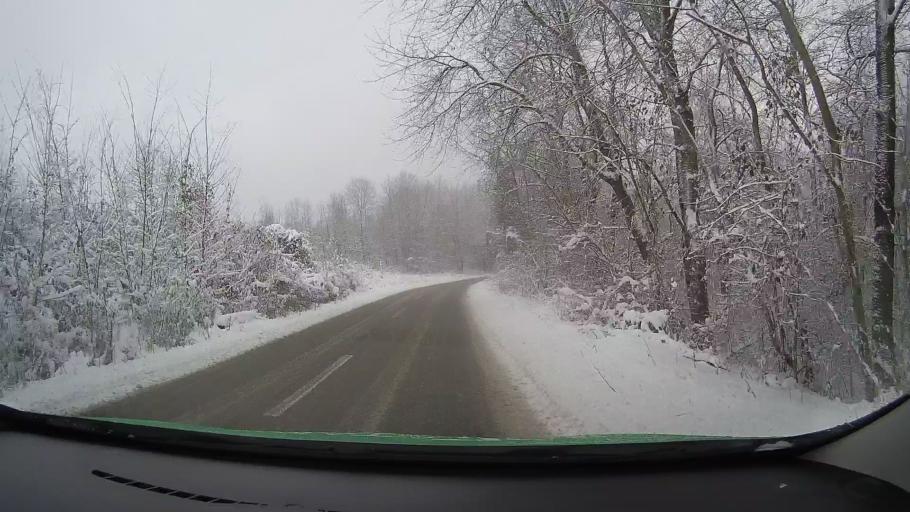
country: RO
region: Hunedoara
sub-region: Comuna Teliucu Inferior
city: Teliucu Inferior
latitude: 45.6810
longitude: 22.9120
